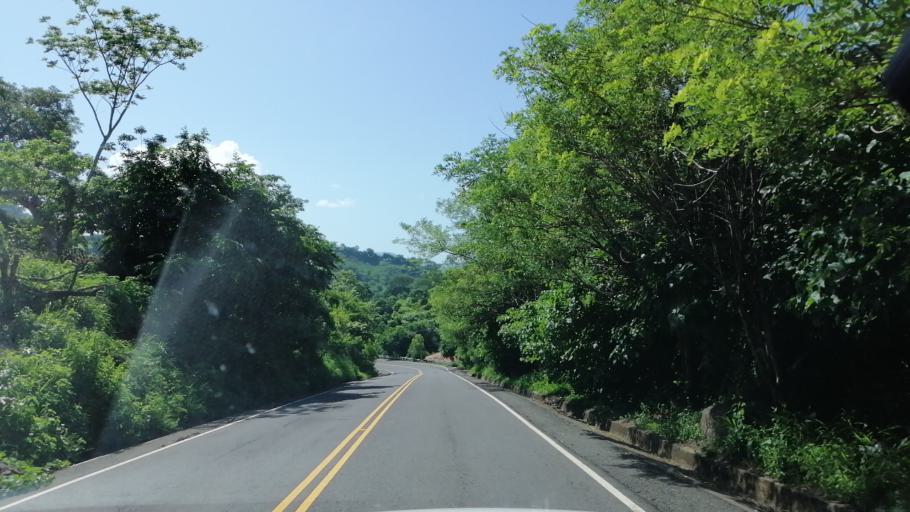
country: HN
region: Lempira
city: La Virtud
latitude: 13.9551
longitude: -88.7491
